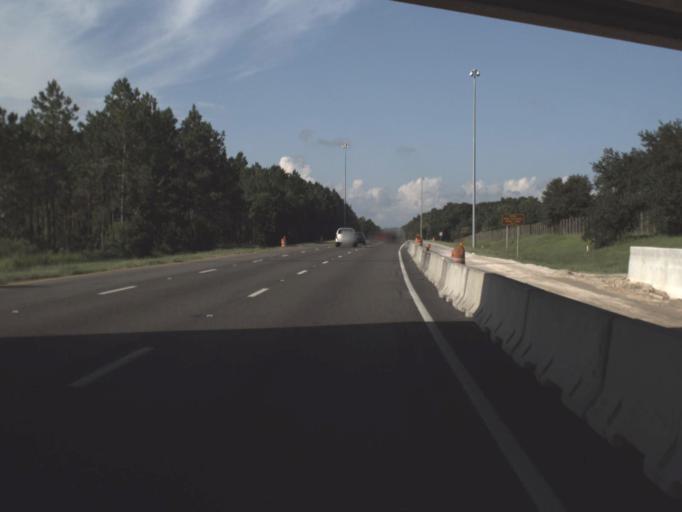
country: US
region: Florida
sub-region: Hillsborough County
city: Pebble Creek
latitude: 28.1713
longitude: -82.3946
